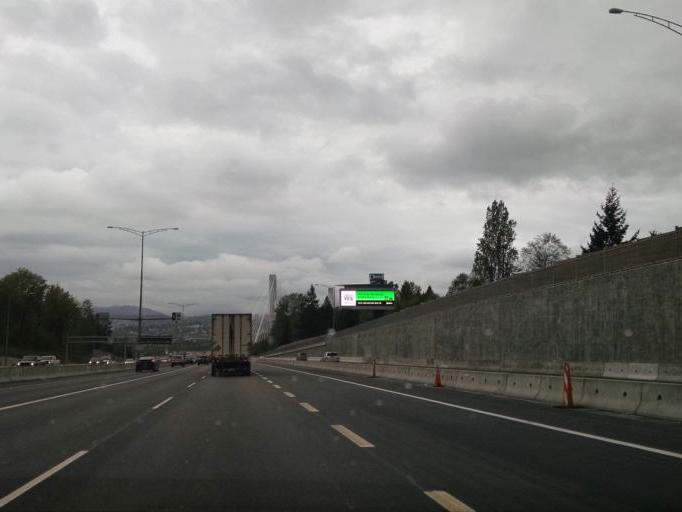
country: CA
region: British Columbia
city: Port Moody
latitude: 49.2068
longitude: -122.8031
